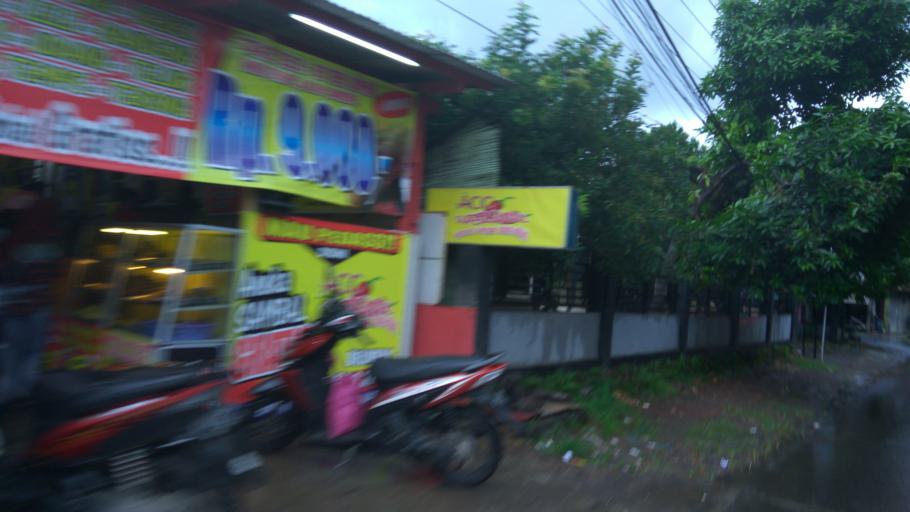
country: ID
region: Central Java
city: Semarang
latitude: -7.0582
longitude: 110.3972
